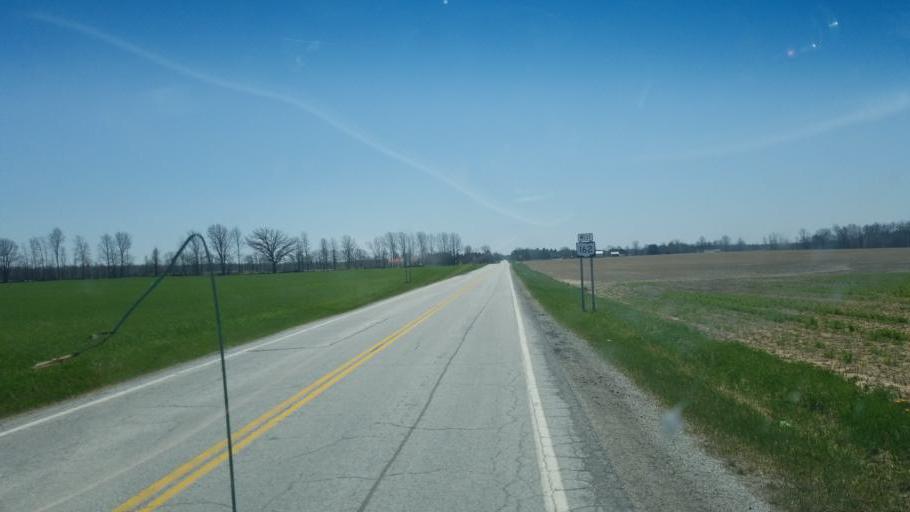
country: US
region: Ohio
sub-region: Huron County
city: New London
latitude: 41.1017
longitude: -82.3480
